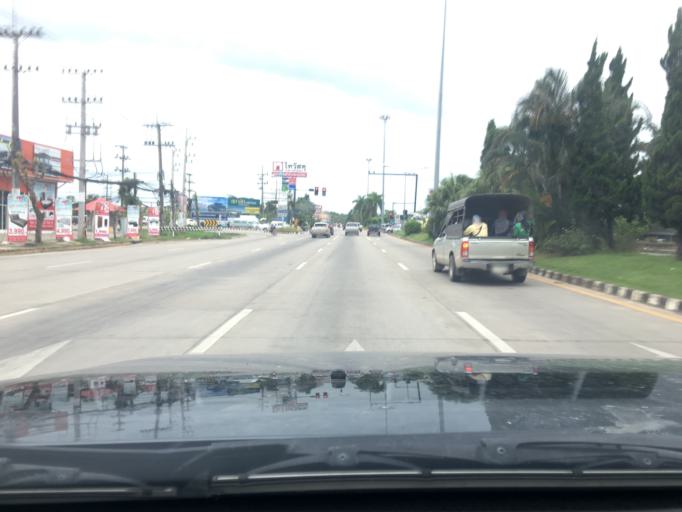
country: TH
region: Chiang Rai
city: Chiang Rai
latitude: 19.8774
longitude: 99.8319
